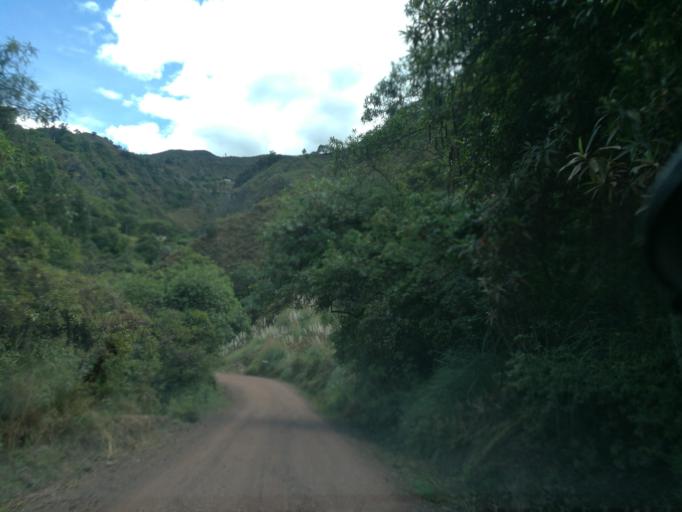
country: CO
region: Boyaca
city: Socota
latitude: 6.1146
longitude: -72.7185
